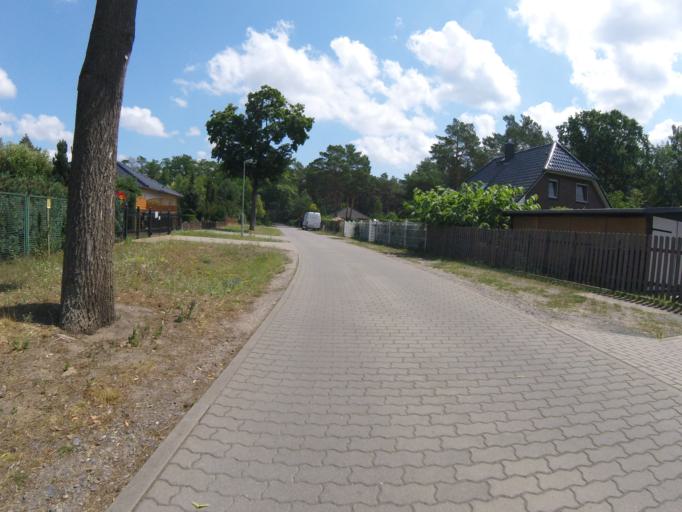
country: DE
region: Brandenburg
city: Bestensee
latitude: 52.2479
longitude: 13.6402
